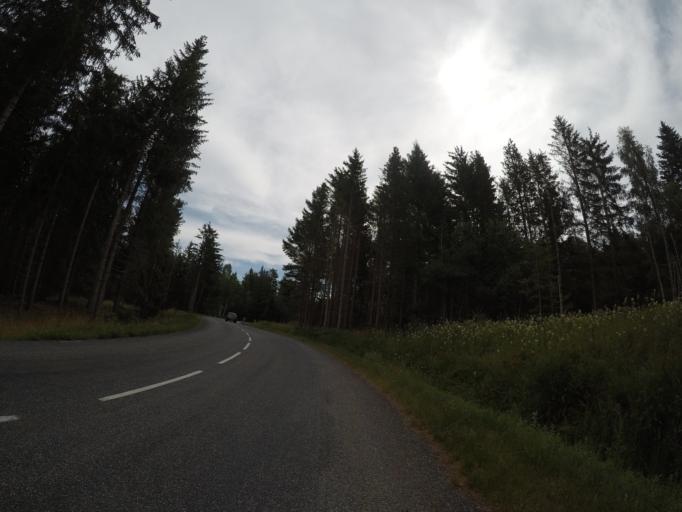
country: ES
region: Catalonia
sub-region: Provincia de Girona
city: Llivia
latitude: 42.4809
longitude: 2.0618
